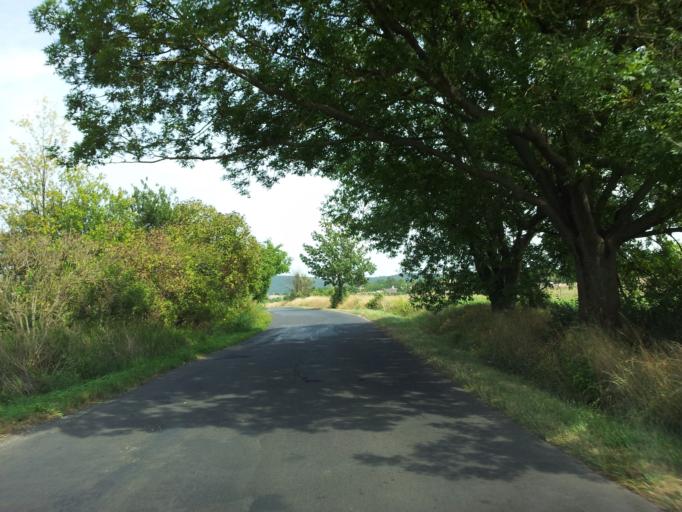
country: HU
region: Veszprem
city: Revfueloep
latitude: 46.8486
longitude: 17.5890
